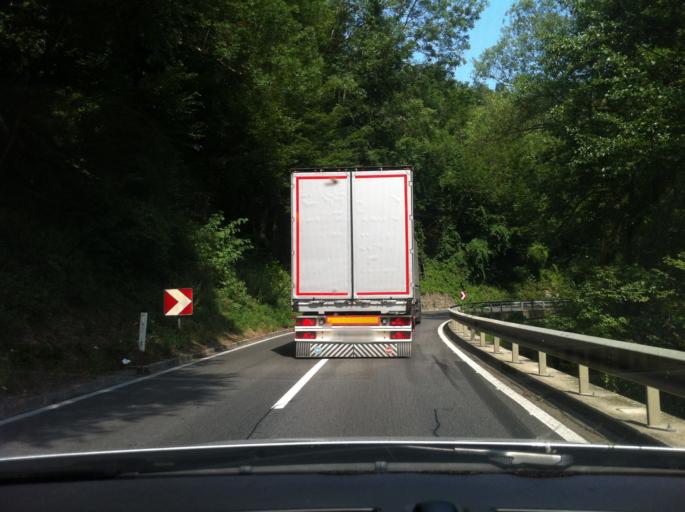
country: AT
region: Styria
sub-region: Politischer Bezirk Hartberg-Fuerstenfeld
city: Stubenberg
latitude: 47.2440
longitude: 15.7854
